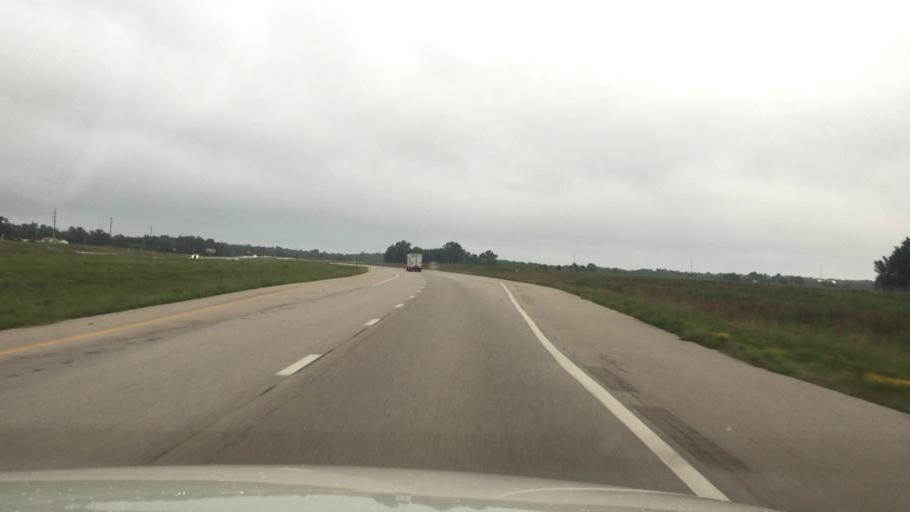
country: US
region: Kansas
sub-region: Montgomery County
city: Coffeyville
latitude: 37.0765
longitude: -95.5894
